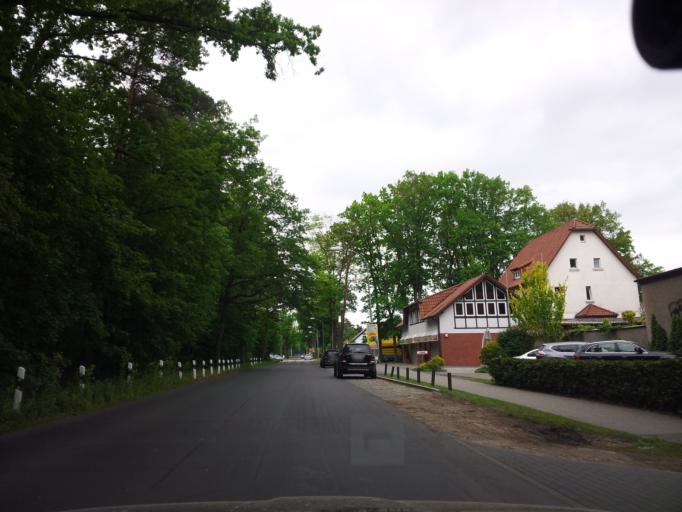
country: DE
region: Brandenburg
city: Falkensee
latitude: 52.5833
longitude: 13.0712
